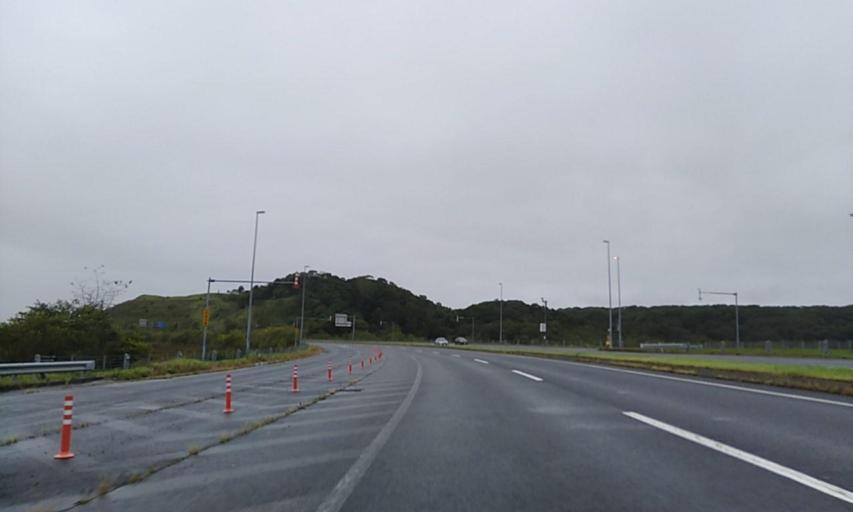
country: JP
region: Hokkaido
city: Kushiro
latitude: 43.0200
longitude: 144.2590
